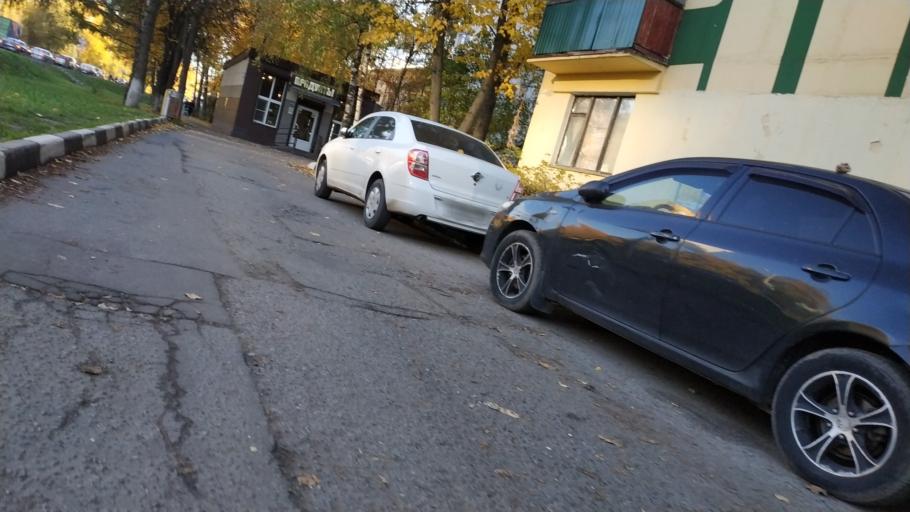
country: RU
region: Moskovskaya
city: Lobnya
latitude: 56.0100
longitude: 37.4604
